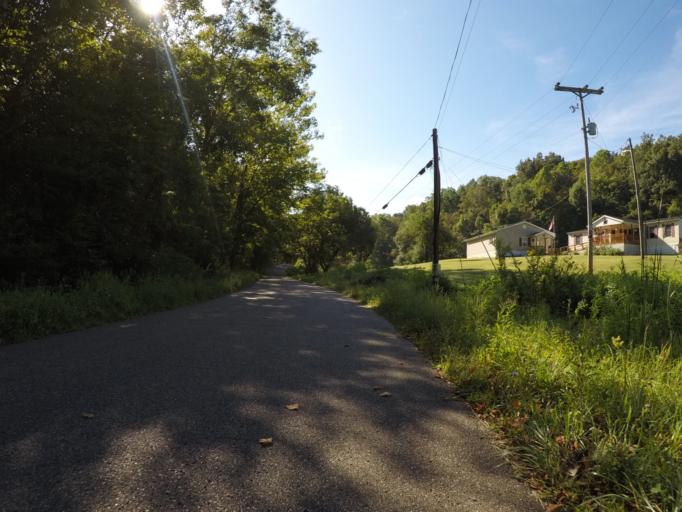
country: US
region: West Virginia
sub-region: Cabell County
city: Huntington
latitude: 38.4777
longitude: -82.4651
